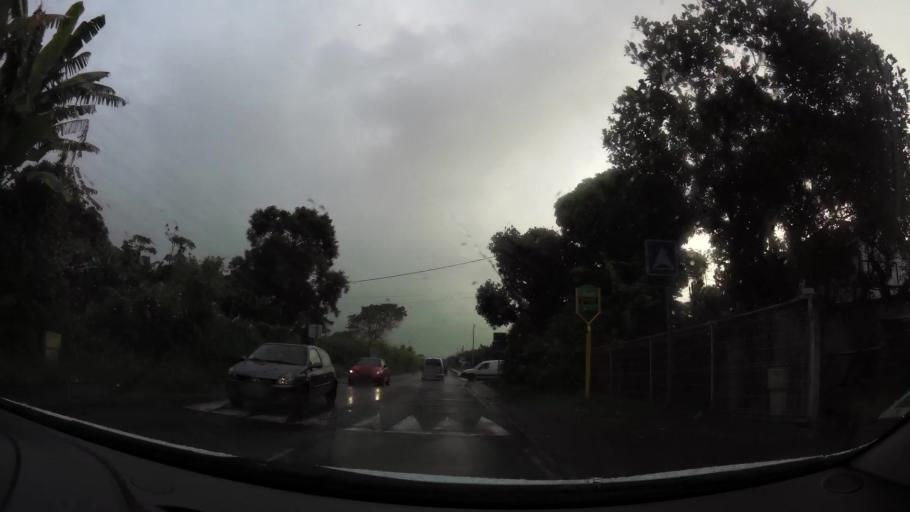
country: RE
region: Reunion
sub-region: Reunion
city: Saint-Andre
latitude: -20.9565
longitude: 55.6670
